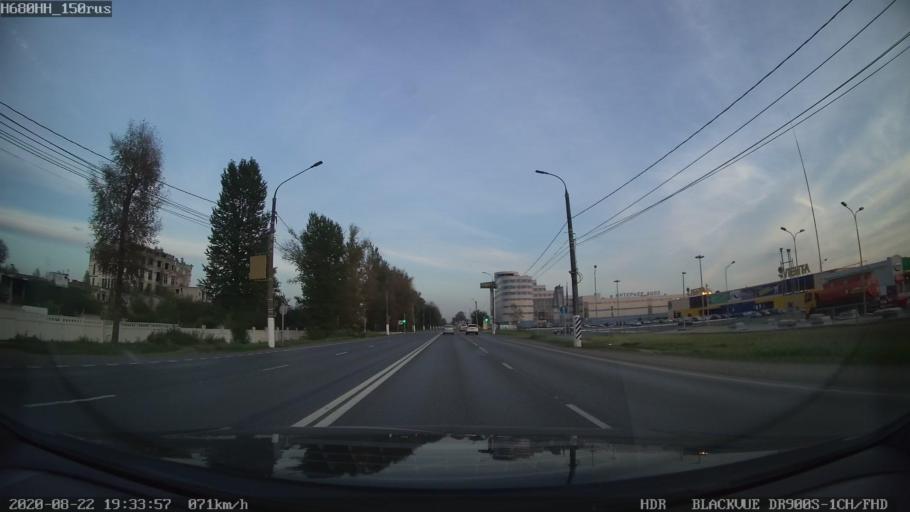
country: RU
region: Tverskaya
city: Tver
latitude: 56.8453
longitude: 35.9486
